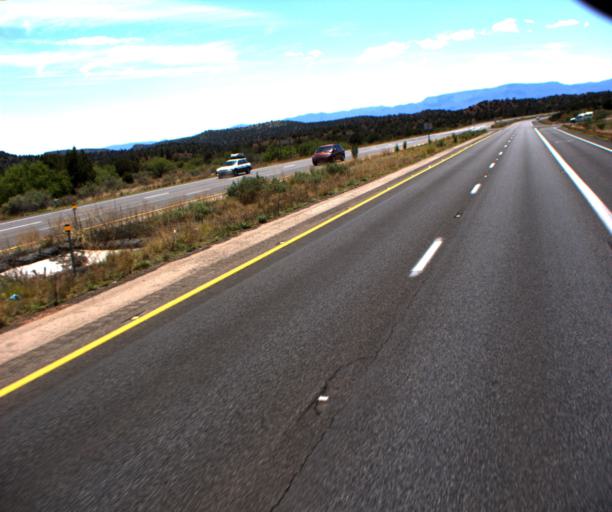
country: US
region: Arizona
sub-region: Yavapai County
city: West Sedona
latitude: 34.8420
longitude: -111.8648
